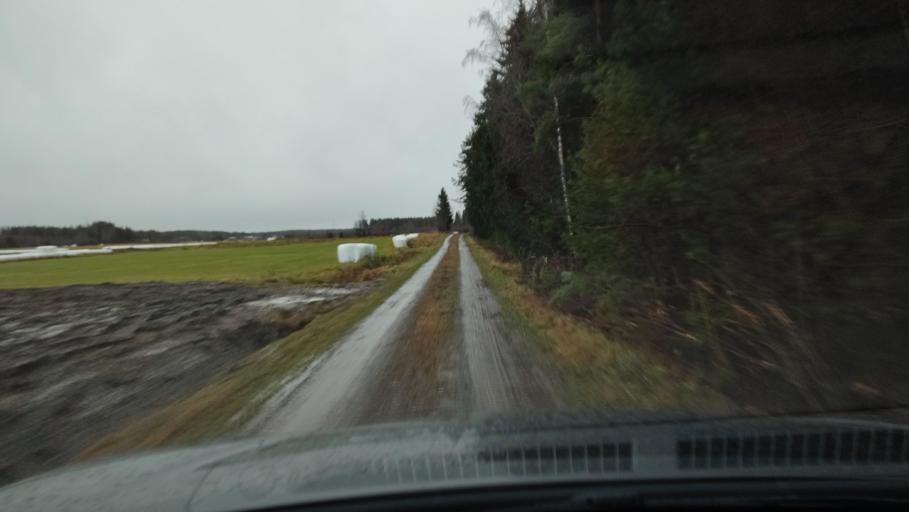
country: FI
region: Southern Ostrobothnia
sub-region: Suupohja
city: Karijoki
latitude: 62.2296
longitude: 21.5517
